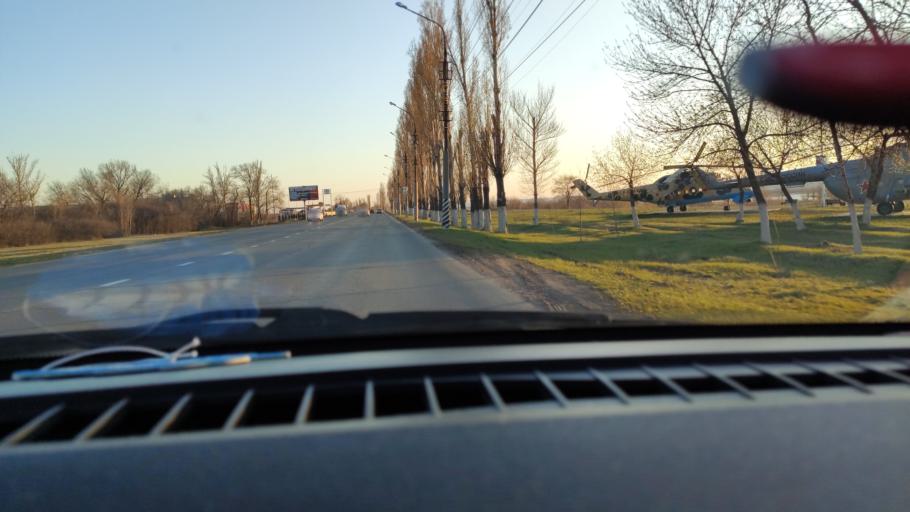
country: RU
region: Saratov
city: Privolzhskiy
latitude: 51.4430
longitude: 46.0705
